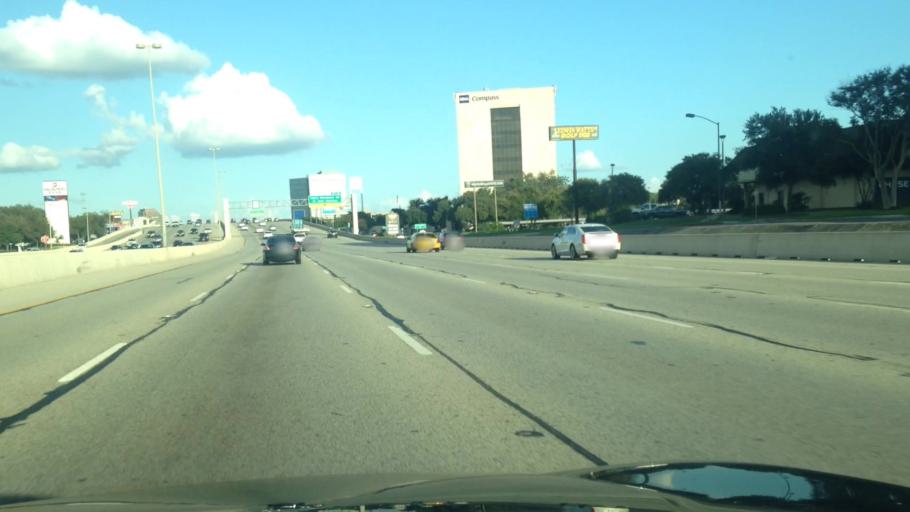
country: US
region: Texas
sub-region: Bexar County
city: Alamo Heights
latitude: 29.5162
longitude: -98.4568
